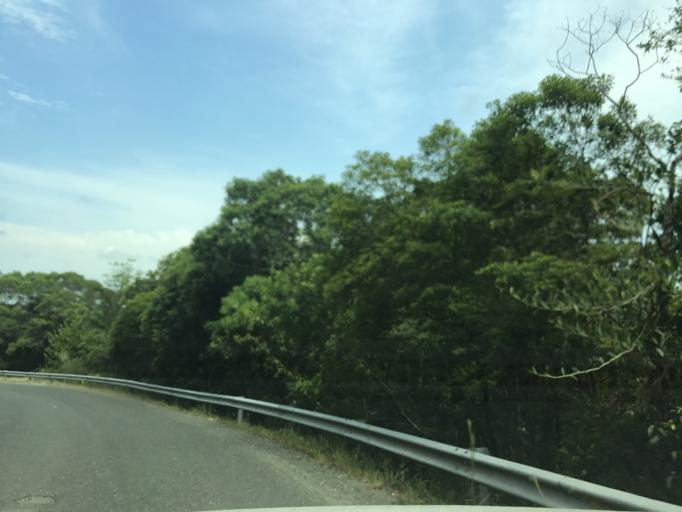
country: GT
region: Izabal
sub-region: Municipio de Los Amates
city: Los Amates
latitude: 15.3855
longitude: -89.0246
